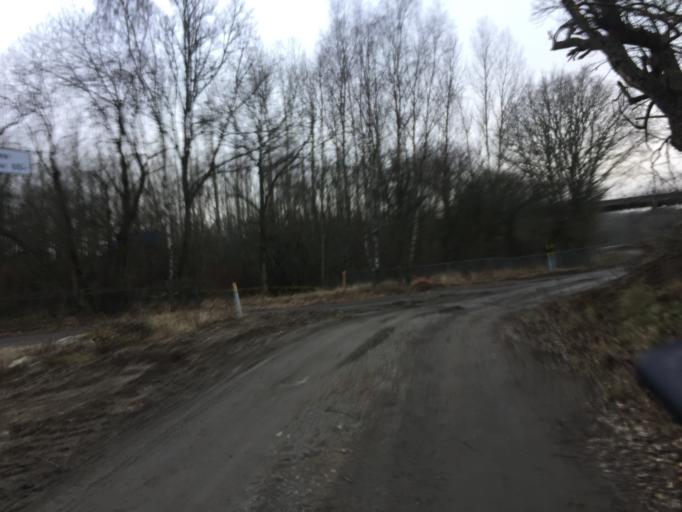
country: SE
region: Blekinge
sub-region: Karlshamns Kommun
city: Morrum
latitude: 56.1763
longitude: 14.7714
